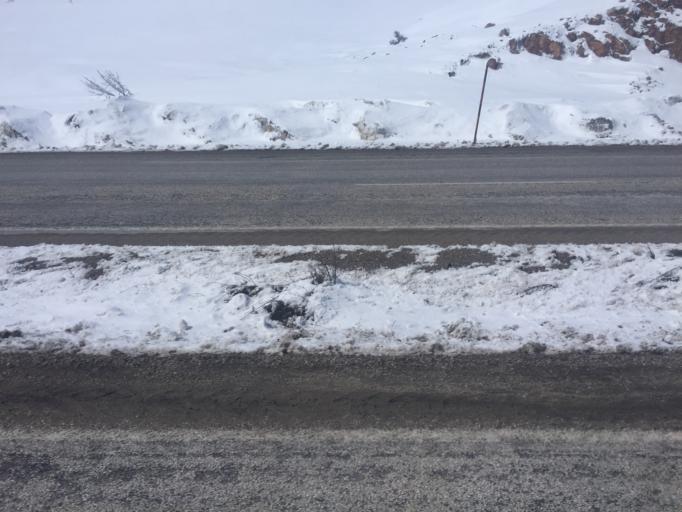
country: TR
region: Kahramanmaras
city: Goksun
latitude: 38.1893
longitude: 36.4569
